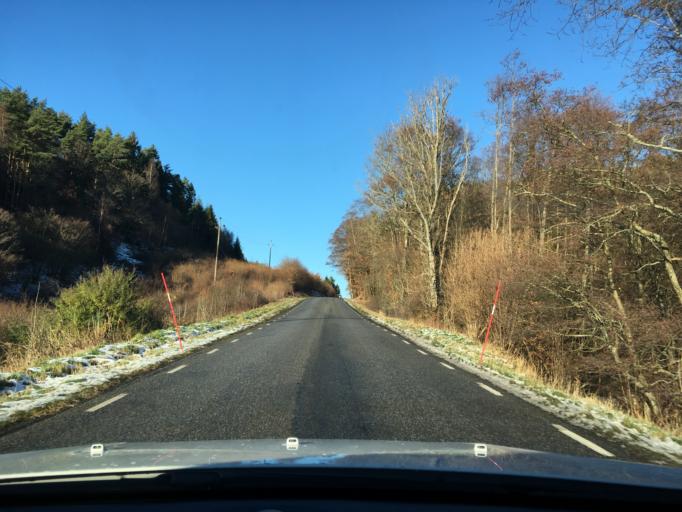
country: SE
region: Vaestra Goetaland
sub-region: Tjorns Kommun
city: Myggenas
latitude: 58.0453
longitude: 11.6758
